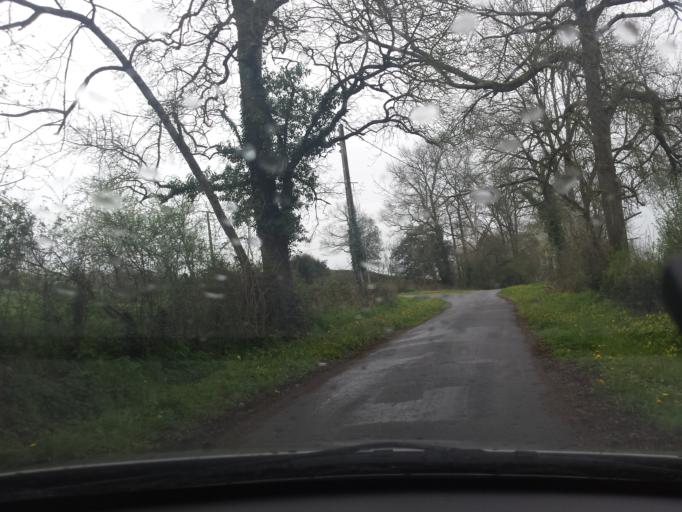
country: FR
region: Pays de la Loire
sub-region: Departement de la Vendee
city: Sainte-Hermine
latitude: 46.5964
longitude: -1.0809
